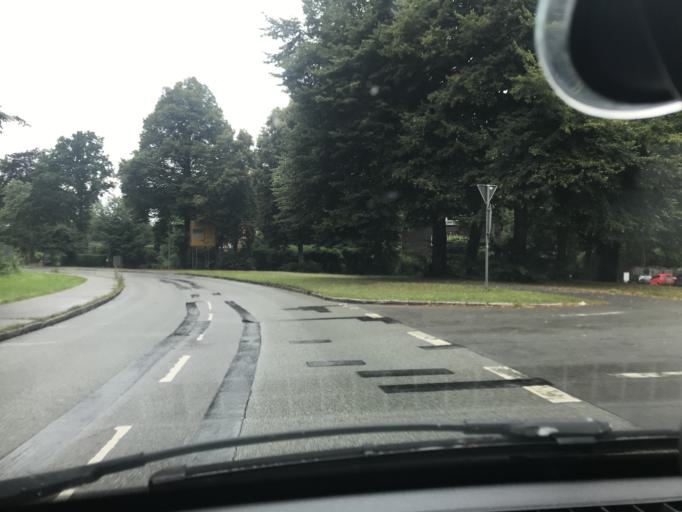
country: DE
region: Schleswig-Holstein
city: Grosshansdorf
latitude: 53.6627
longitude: 10.2561
